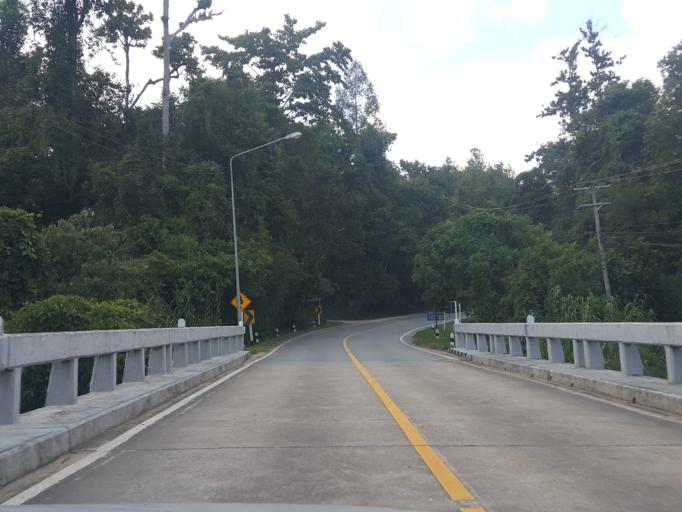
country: TH
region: Chiang Mai
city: Chom Thong
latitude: 18.5297
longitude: 98.6085
